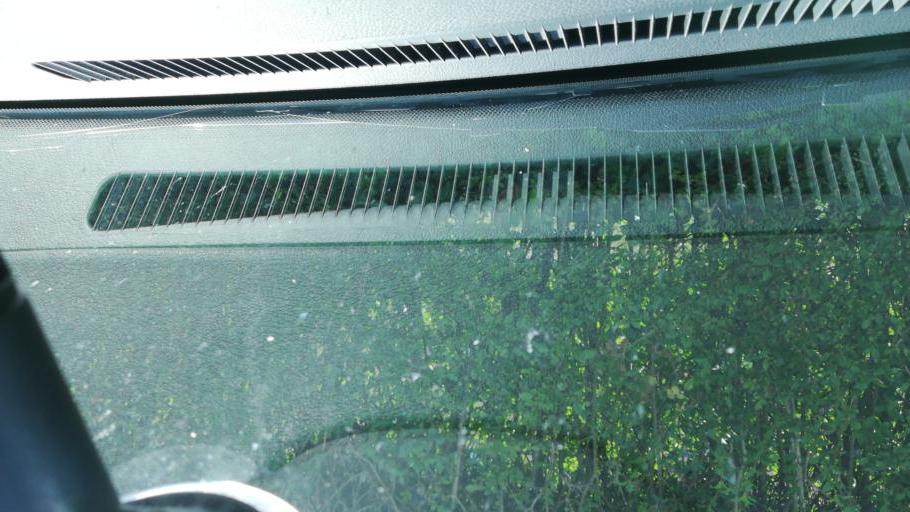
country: DE
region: Bavaria
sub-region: Regierungsbezirk Unterfranken
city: Schollkrippen
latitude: 50.0859
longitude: 9.2476
